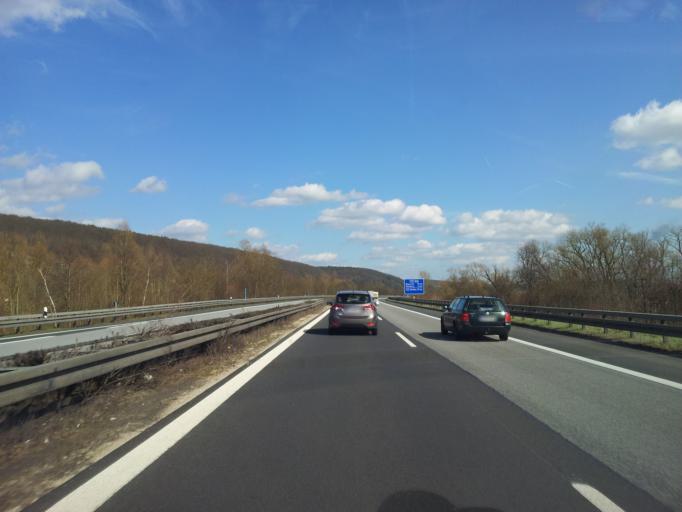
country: DE
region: Bavaria
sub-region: Regierungsbezirk Unterfranken
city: Ebelsbach
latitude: 49.9779
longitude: 10.6778
